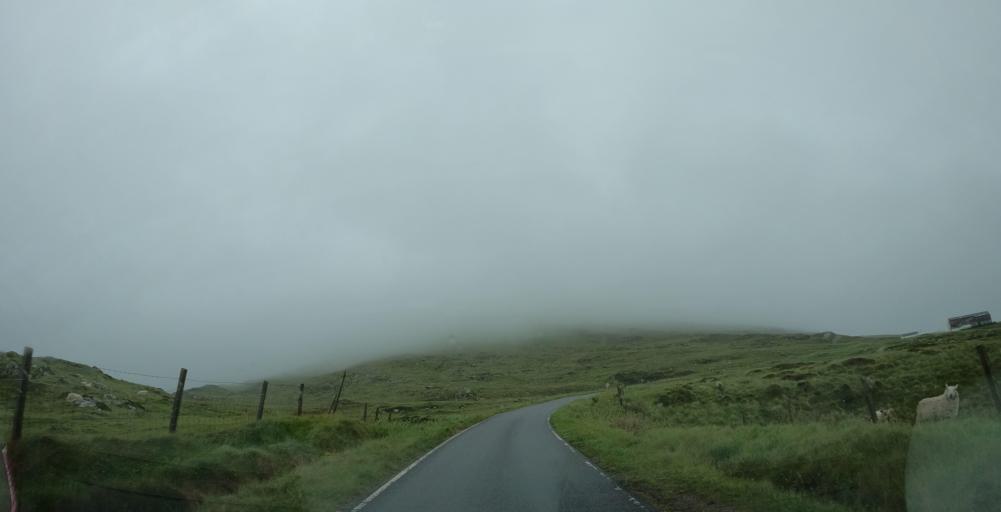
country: GB
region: Scotland
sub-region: Eilean Siar
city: Barra
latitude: 56.9592
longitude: -7.4701
